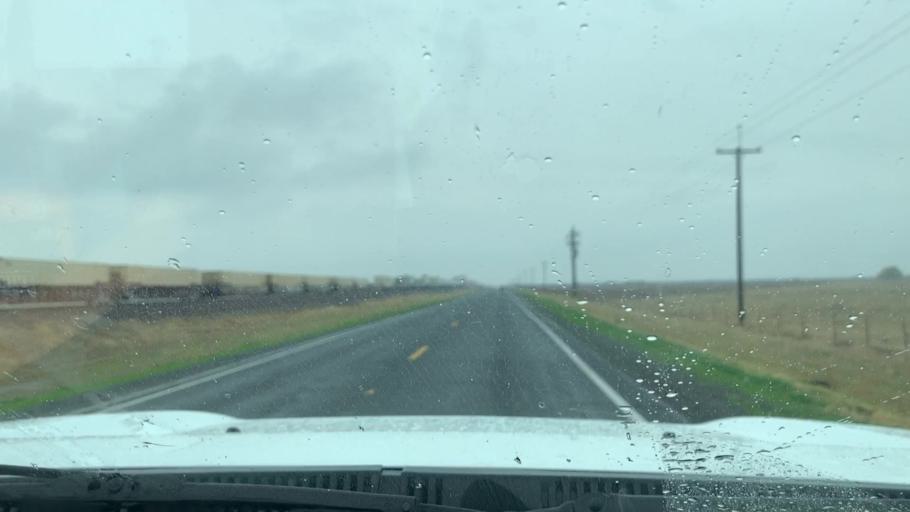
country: US
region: California
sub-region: Tulare County
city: Alpaugh
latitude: 35.9135
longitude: -119.4214
